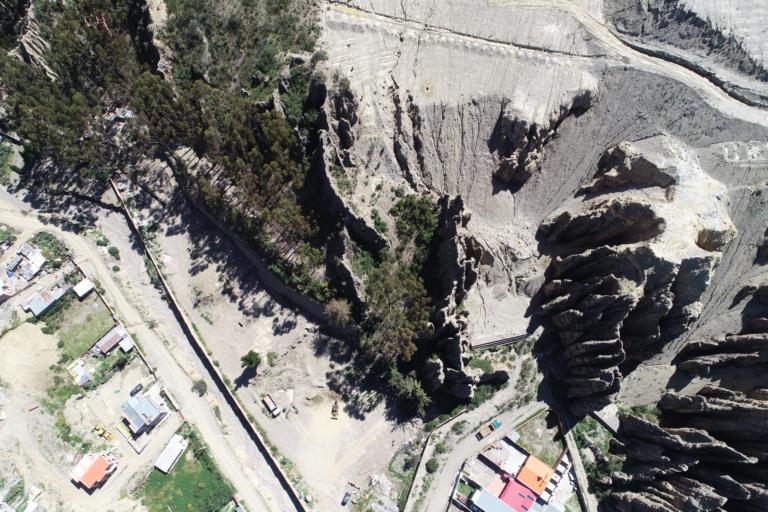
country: BO
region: La Paz
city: La Paz
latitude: -16.5082
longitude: -68.0577
